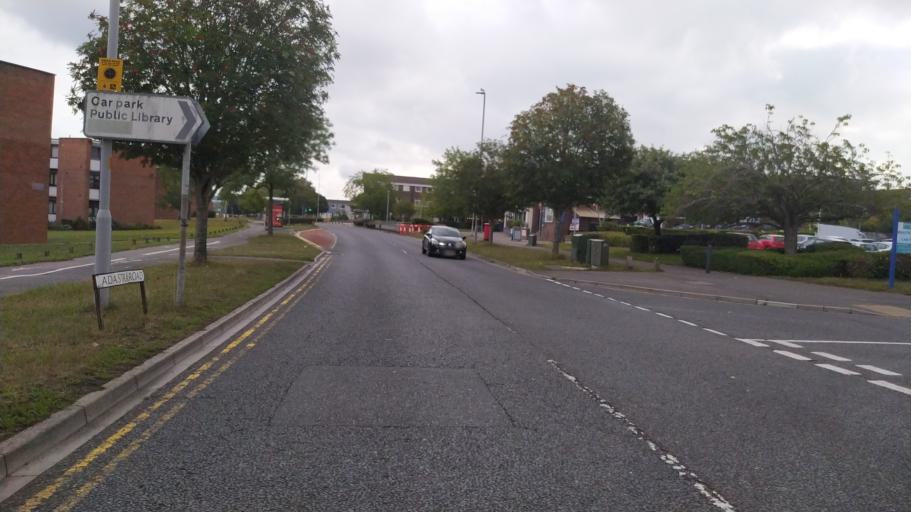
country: GB
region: England
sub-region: Poole
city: Canford Heath
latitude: 50.7417
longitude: -1.9664
